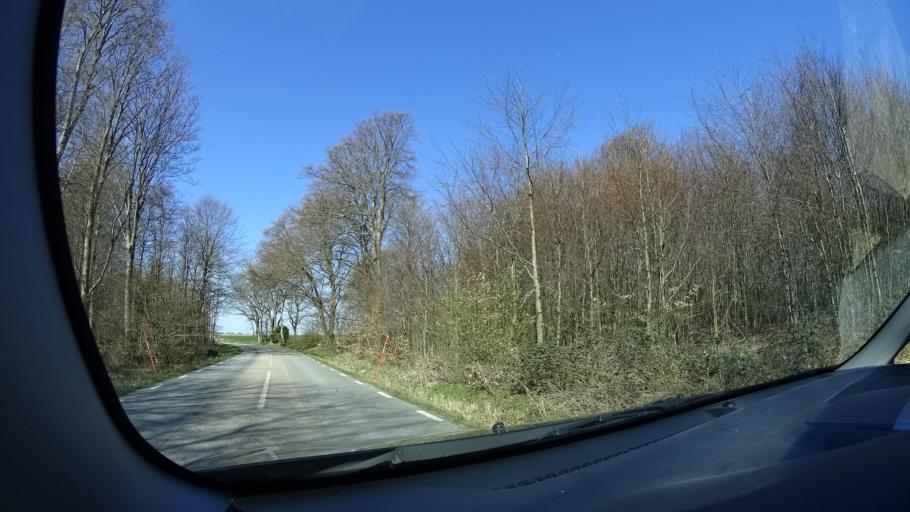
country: SE
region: Skane
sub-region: Hoganas Kommun
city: Hoganas
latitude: 56.2682
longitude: 12.5479
